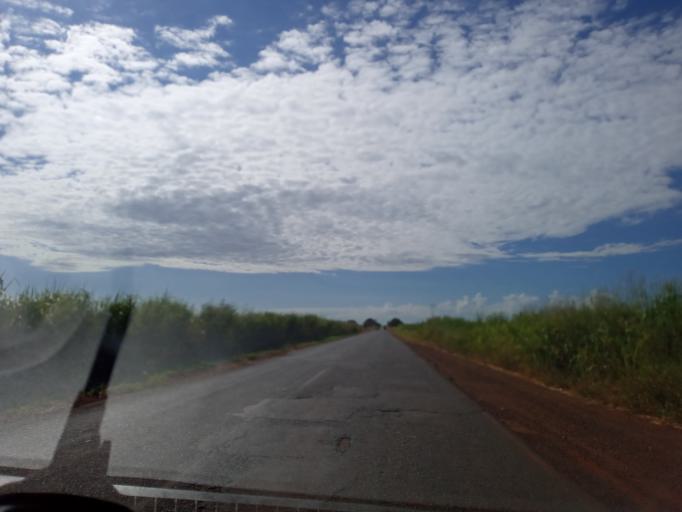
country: BR
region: Goias
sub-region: Itumbiara
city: Itumbiara
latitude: -18.4599
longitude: -49.1400
